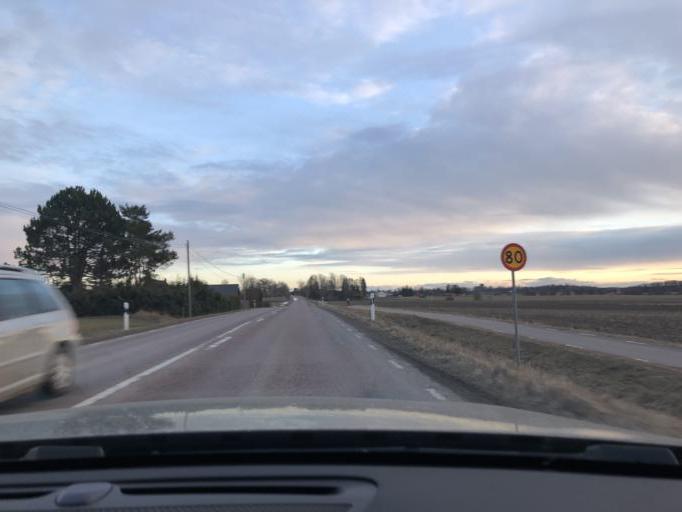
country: SE
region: Uppsala
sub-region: Uppsala Kommun
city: Gamla Uppsala
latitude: 59.9195
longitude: 17.6421
